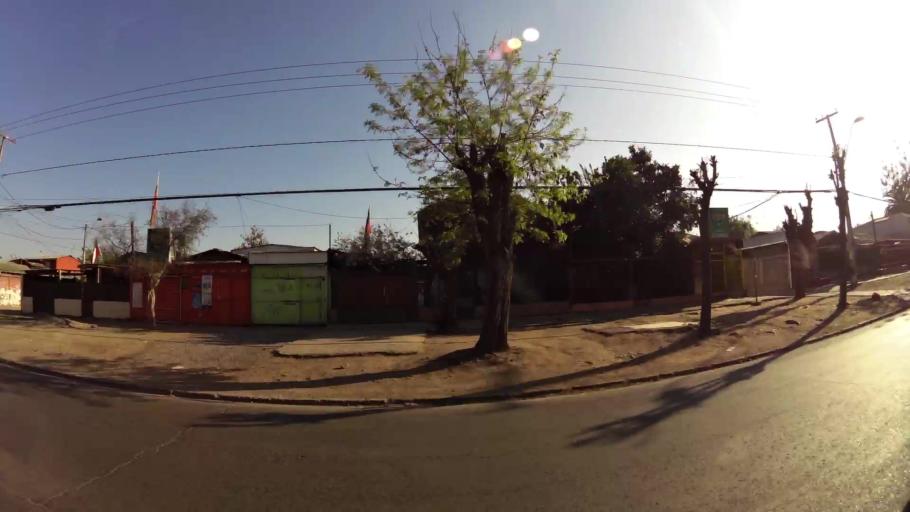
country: CL
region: Santiago Metropolitan
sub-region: Provincia de Santiago
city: Santiago
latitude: -33.3809
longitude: -70.6523
